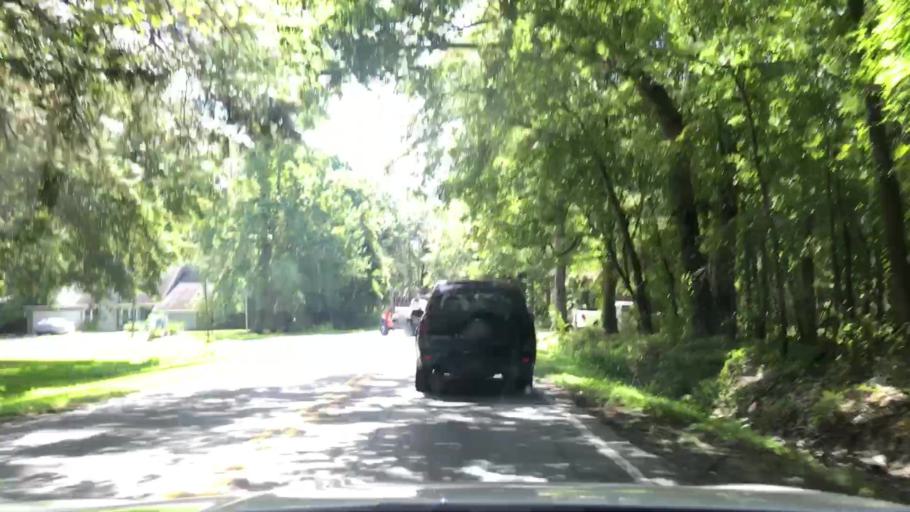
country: US
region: South Carolina
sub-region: Charleston County
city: Shell Point
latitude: 32.8392
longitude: -80.0522
